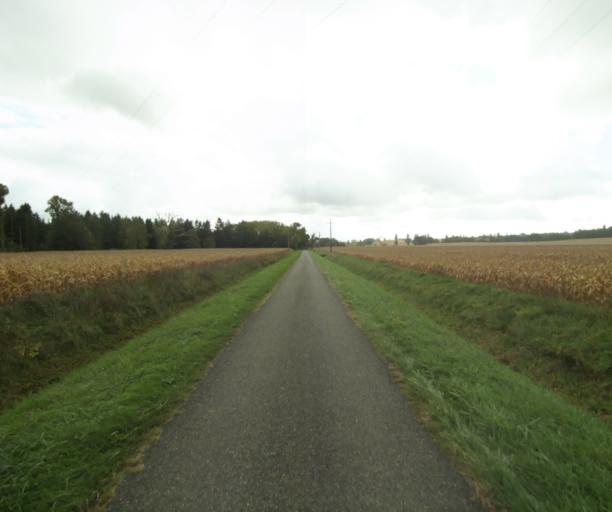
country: FR
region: Midi-Pyrenees
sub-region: Departement du Gers
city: Cazaubon
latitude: 43.8617
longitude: -0.0062
